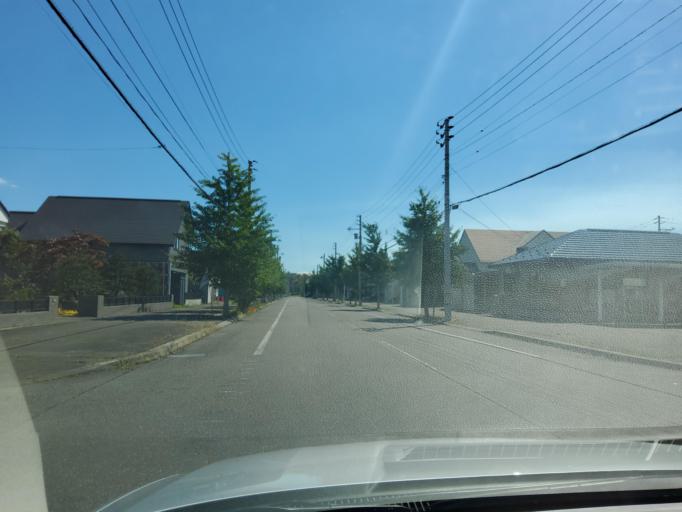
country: JP
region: Hokkaido
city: Obihiro
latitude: 42.9427
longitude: 143.2197
